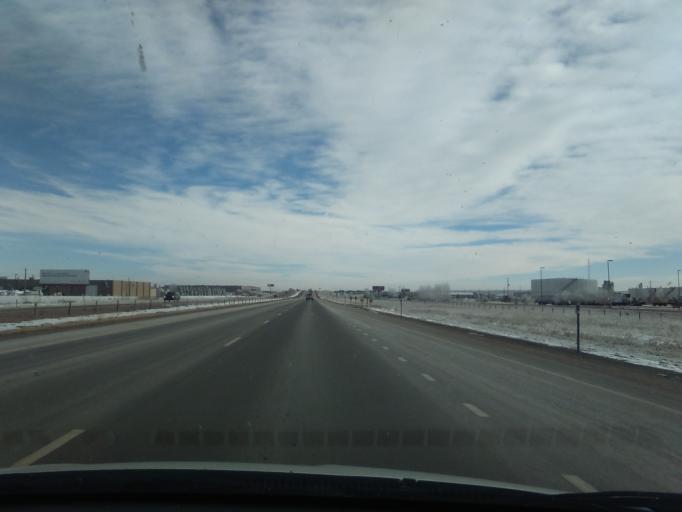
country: US
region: Wyoming
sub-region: Laramie County
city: Fox Farm-College
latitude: 41.1241
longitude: -104.7591
